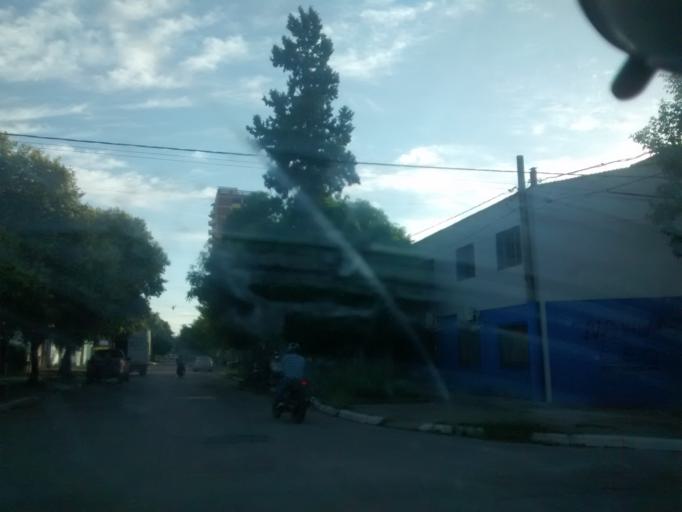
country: AR
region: Chaco
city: Resistencia
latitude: -27.4629
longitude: -58.9768
